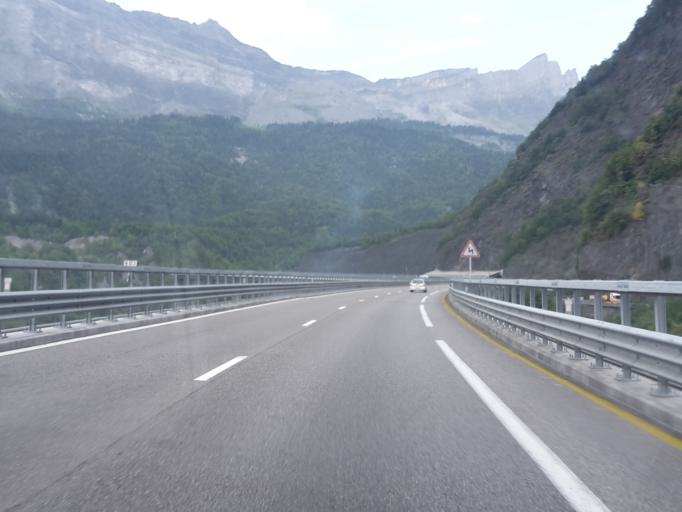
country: FR
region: Rhone-Alpes
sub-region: Departement de la Haute-Savoie
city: Saint-Gervais-les-Bains
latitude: 45.9245
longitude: 6.7316
